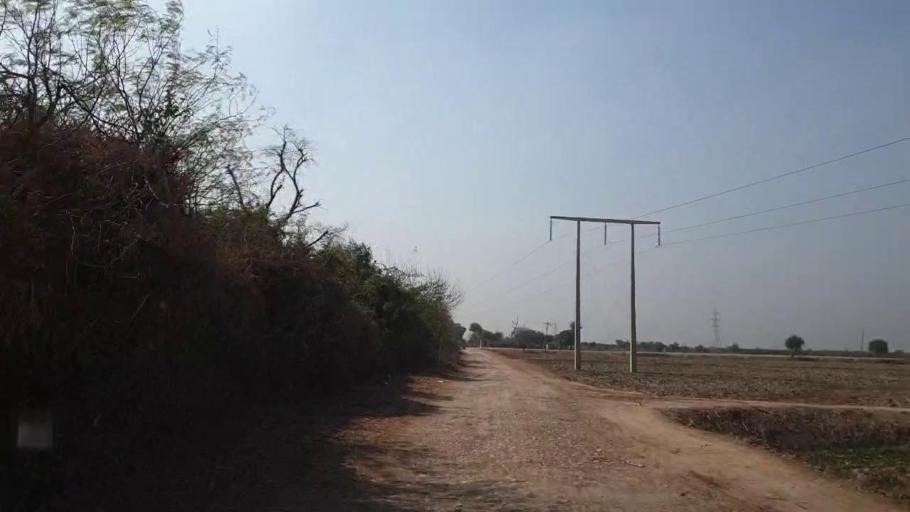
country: PK
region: Sindh
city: Tando Allahyar
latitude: 25.4960
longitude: 68.8243
